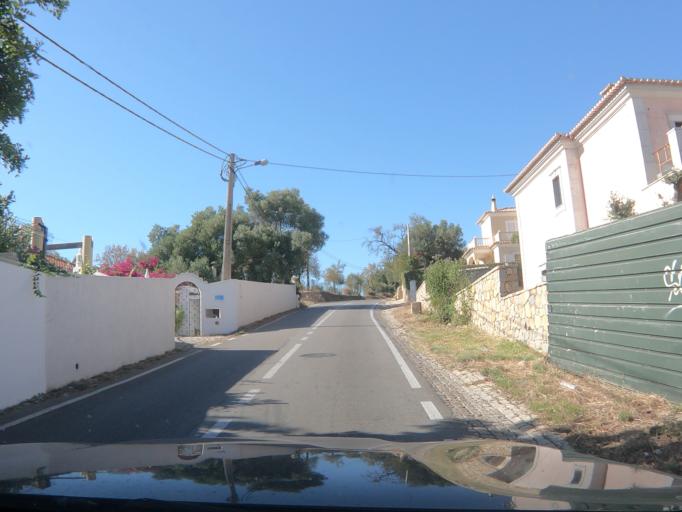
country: PT
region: Faro
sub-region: Loule
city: Almancil
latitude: 37.1066
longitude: -8.0417
